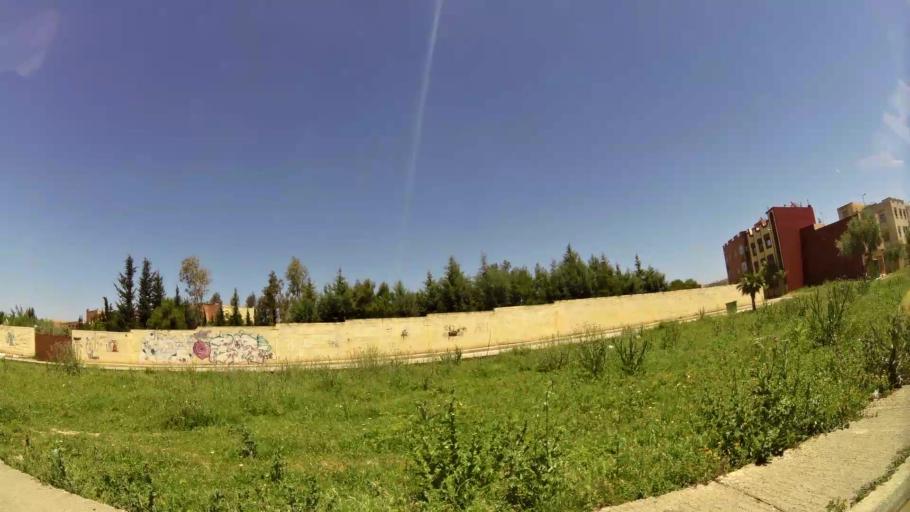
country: MA
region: Meknes-Tafilalet
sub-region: Meknes
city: Meknes
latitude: 33.8667
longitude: -5.5758
